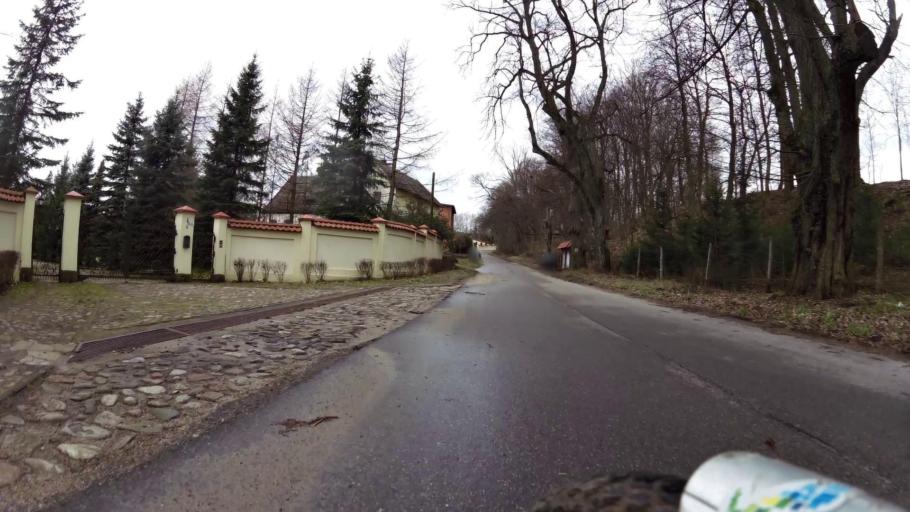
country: PL
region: Pomeranian Voivodeship
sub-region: Powiat bytowski
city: Kolczyglowy
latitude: 54.2408
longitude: 17.2424
